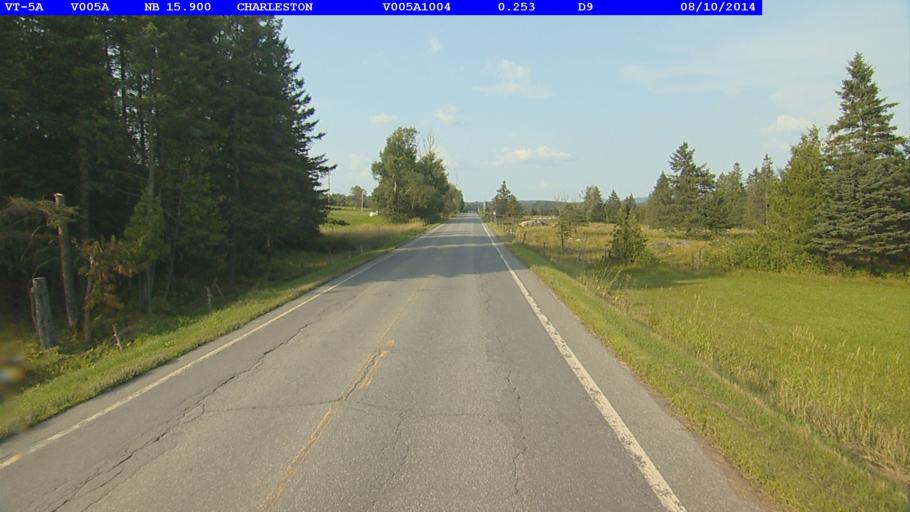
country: US
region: Vermont
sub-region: Orleans County
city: Newport
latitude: 44.8380
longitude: -72.0632
